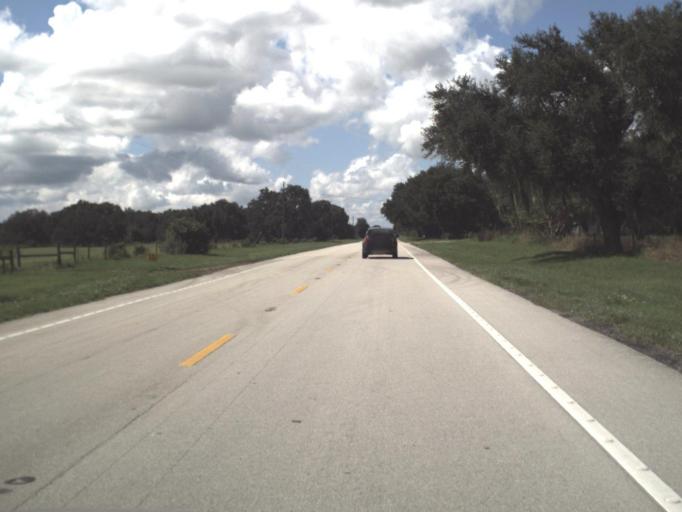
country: US
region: Florida
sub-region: DeSoto County
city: Arcadia
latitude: 27.2746
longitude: -82.0142
